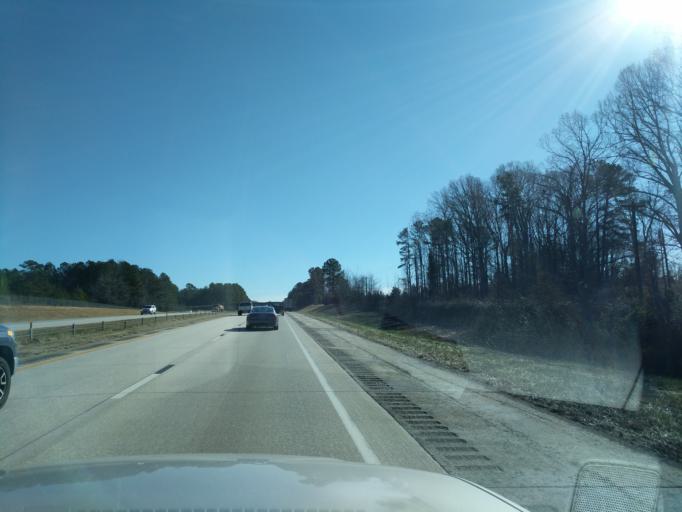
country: US
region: South Carolina
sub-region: Laurens County
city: Watts Mills
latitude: 34.5329
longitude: -81.9367
